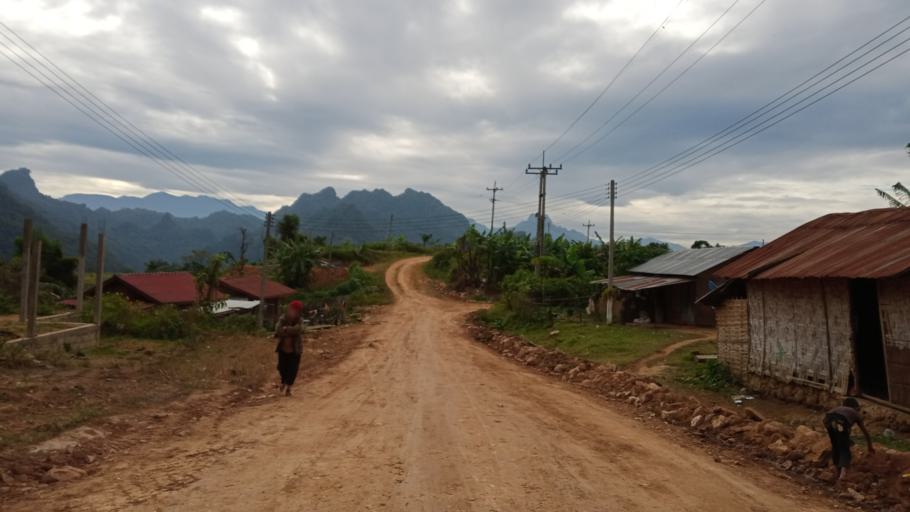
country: LA
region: Xiangkhoang
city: Phonsavan
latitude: 19.1113
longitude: 102.9260
